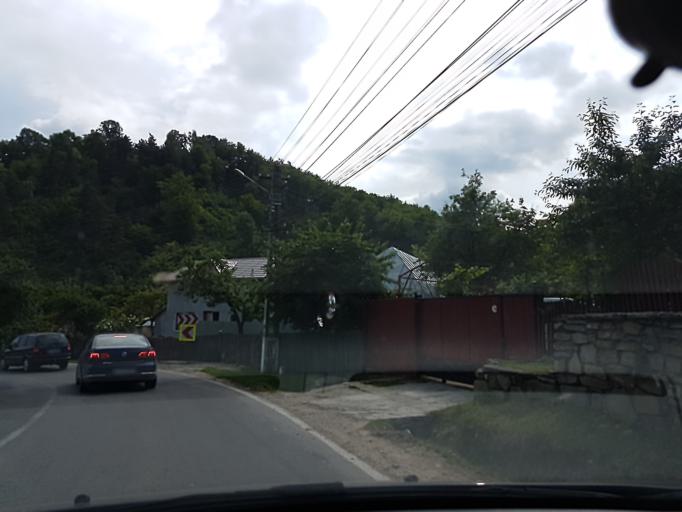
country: RO
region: Prahova
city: Maneciu
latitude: 45.3122
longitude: 25.9895
